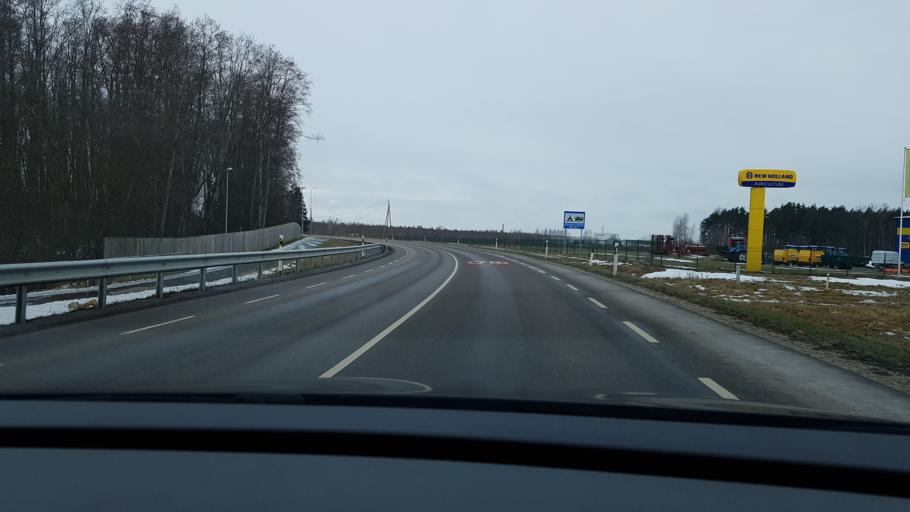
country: EE
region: Paernumaa
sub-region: Sauga vald
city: Sauga
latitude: 58.4326
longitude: 24.4400
